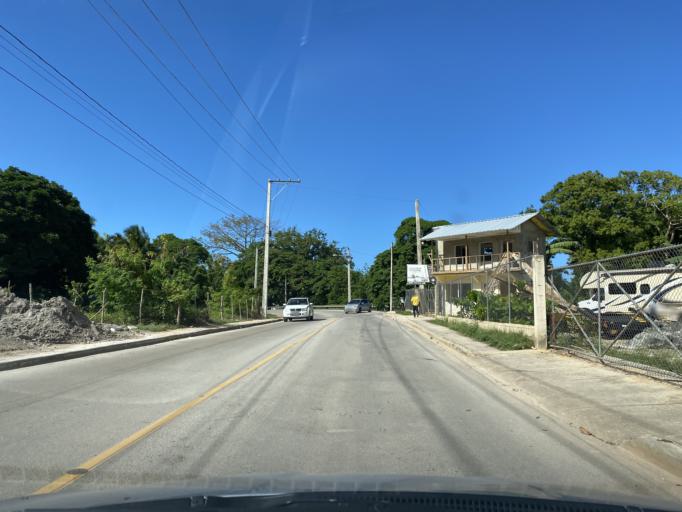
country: DO
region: Samana
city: Las Terrenas
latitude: 19.3056
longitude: -69.5502
